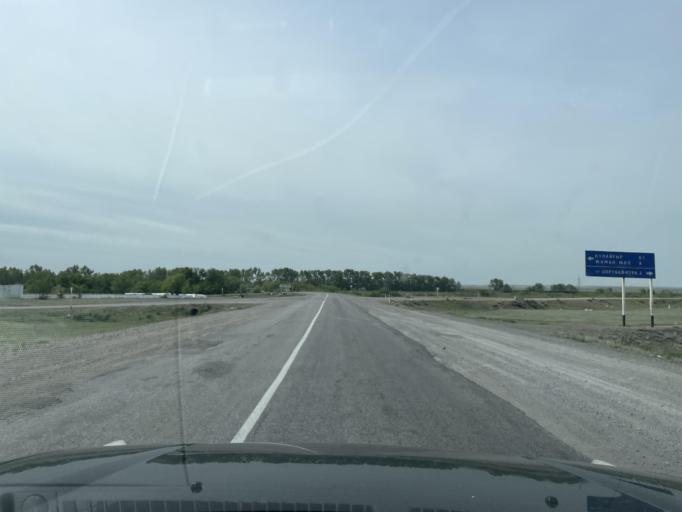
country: KZ
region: Qaraghandy
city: Abay
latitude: 49.4236
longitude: 72.9107
